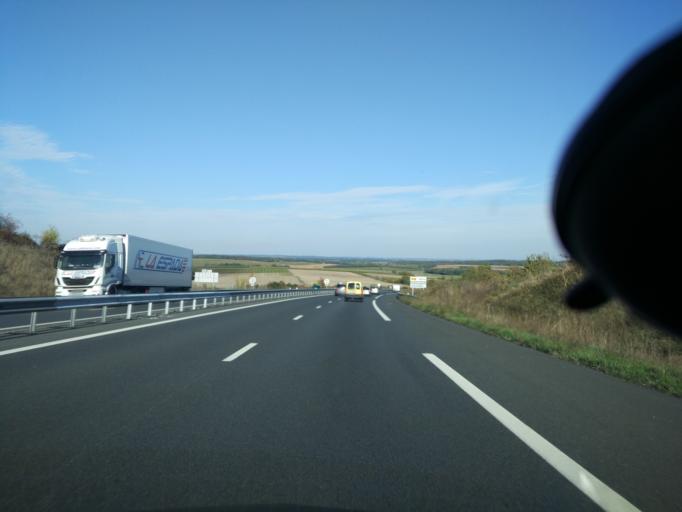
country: FR
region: Poitou-Charentes
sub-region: Departement de la Charente
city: Chateauneuf-sur-Charente
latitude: 45.5410
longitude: -0.0430
